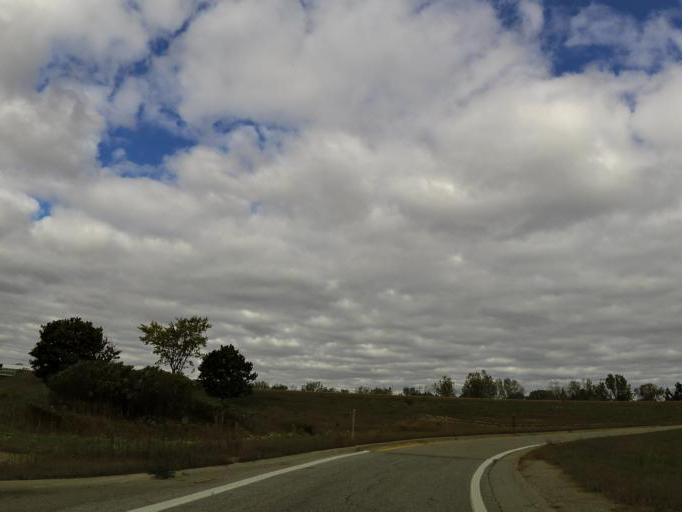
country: US
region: Michigan
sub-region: Genesee County
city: Swartz Creek
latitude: 42.9730
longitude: -83.7630
